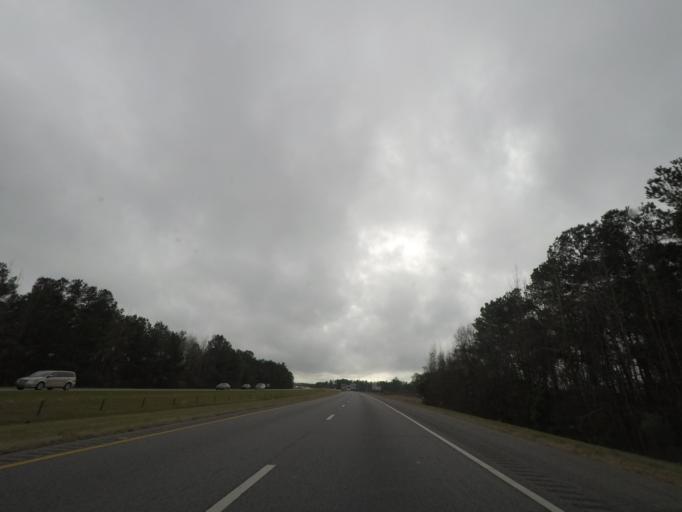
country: US
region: South Carolina
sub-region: Orangeburg County
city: Holly Hill
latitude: 33.4001
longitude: -80.5114
